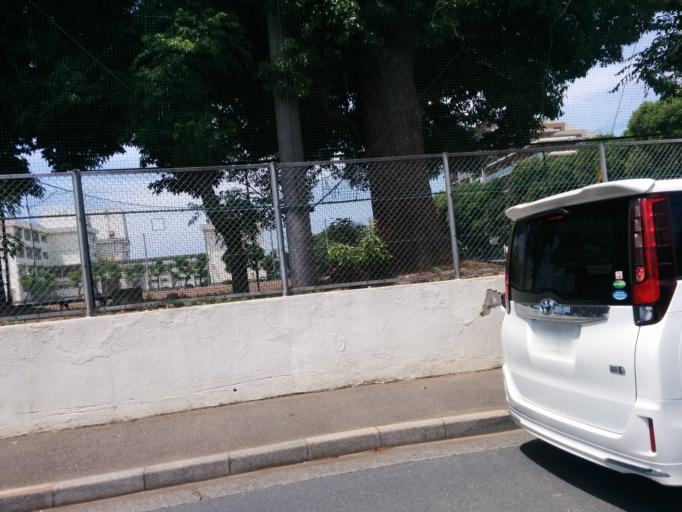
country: JP
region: Tokyo
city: Higashimurayama-shi
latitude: 35.7601
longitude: 139.4783
